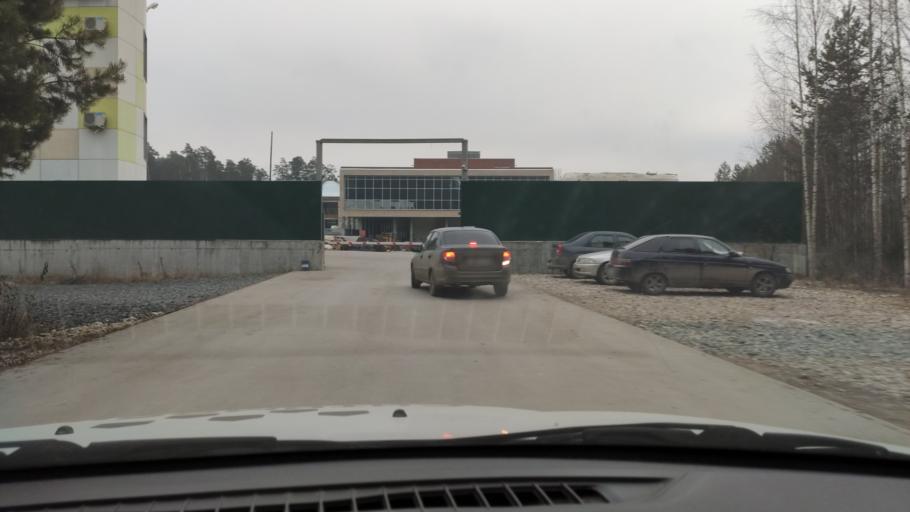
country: RU
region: Perm
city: Kondratovo
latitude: 58.0470
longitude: 56.1492
